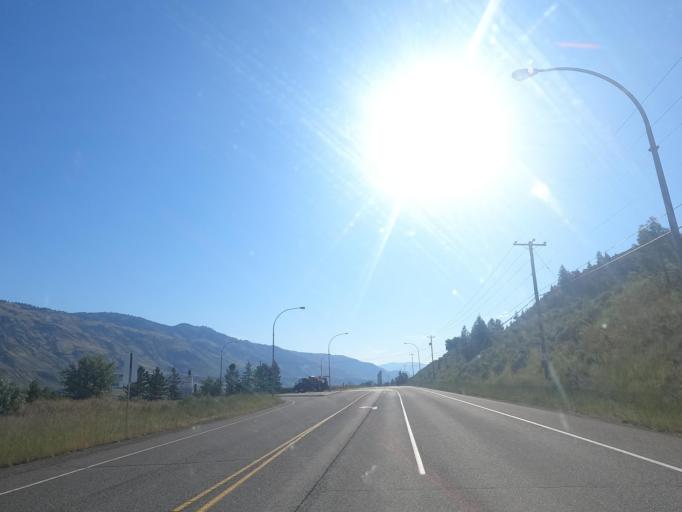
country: CA
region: British Columbia
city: Kamloops
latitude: 50.6528
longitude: -120.0694
